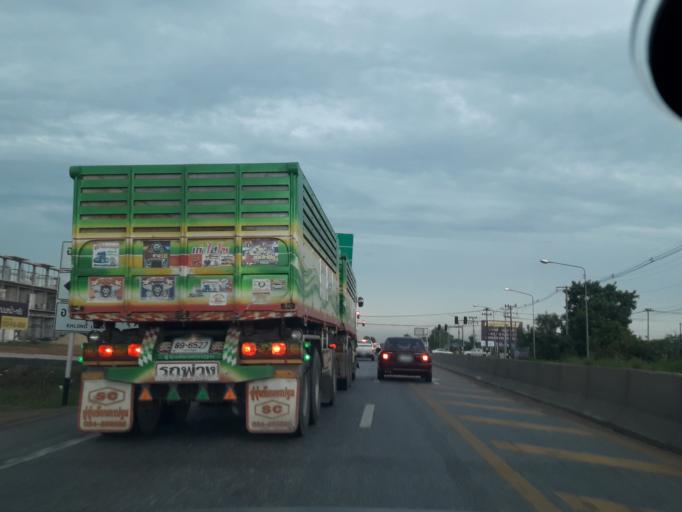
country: TH
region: Pathum Thani
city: Nong Suea
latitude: 14.1330
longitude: 100.7473
